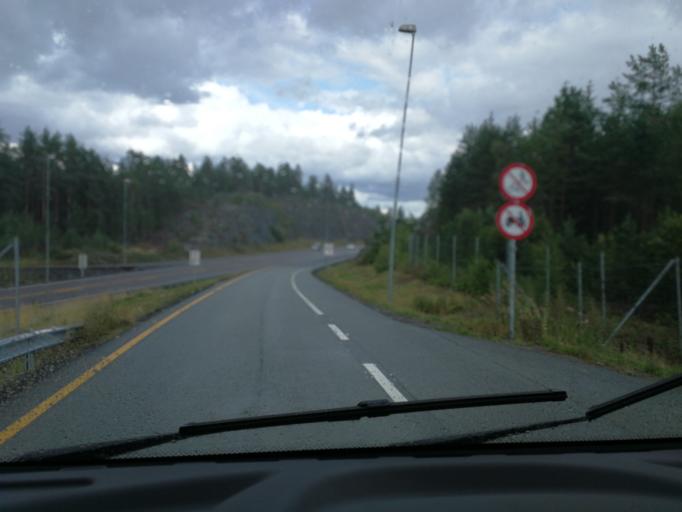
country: NO
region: Ostfold
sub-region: Marker
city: Orje
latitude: 59.5394
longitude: 11.5383
